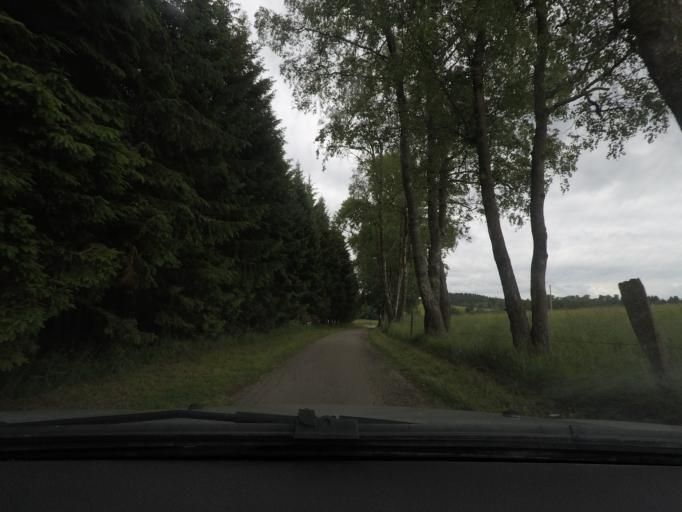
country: BE
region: Wallonia
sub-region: Province du Luxembourg
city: Leglise
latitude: 49.8329
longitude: 5.5192
